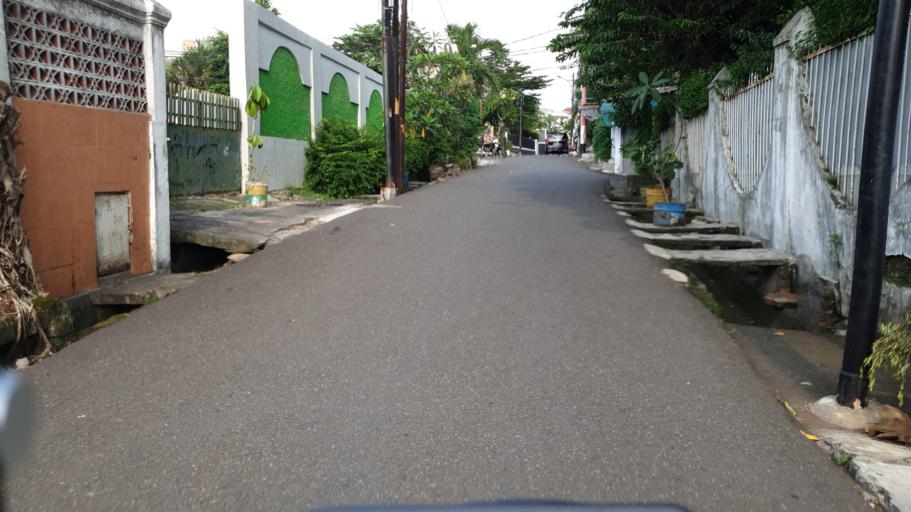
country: ID
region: Banten
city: South Tangerang
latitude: -6.2758
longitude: 106.7949
